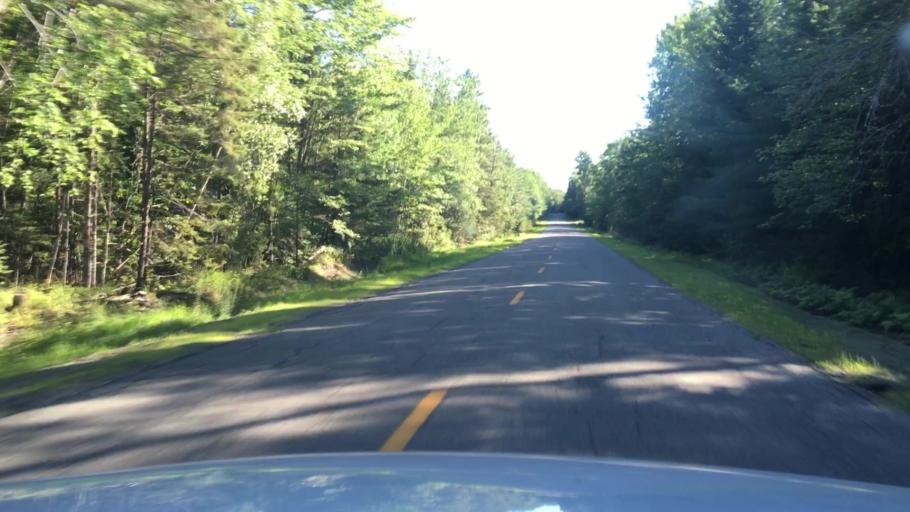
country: US
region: Maine
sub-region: Penobscot County
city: Enfield
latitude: 45.2172
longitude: -68.5840
